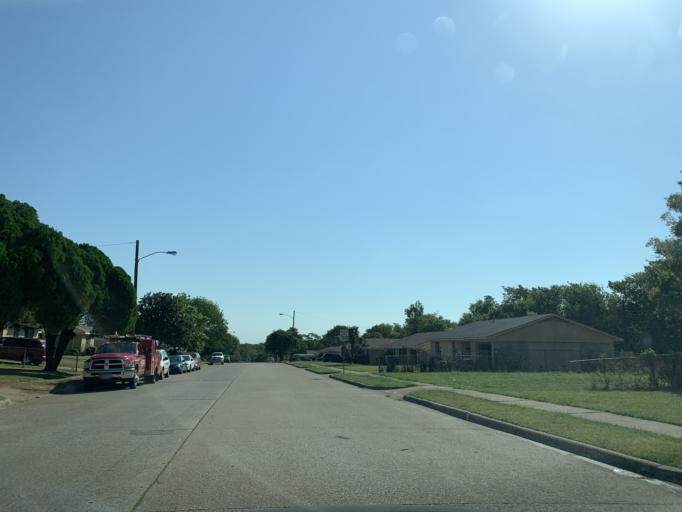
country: US
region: Texas
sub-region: Dallas County
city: Hutchins
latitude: 32.6654
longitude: -96.7551
